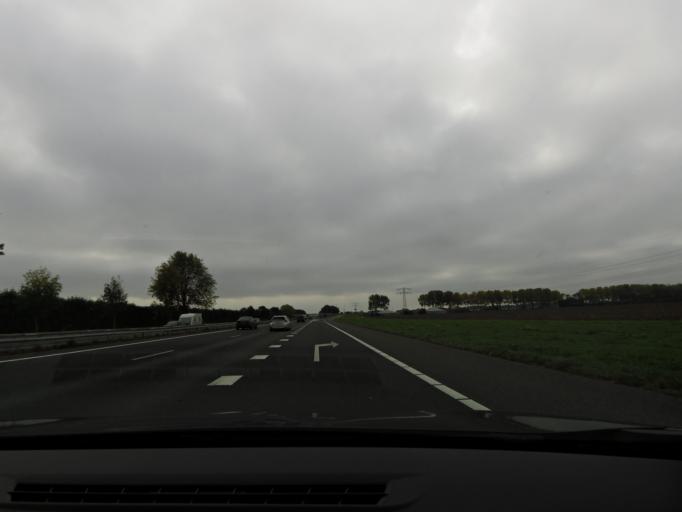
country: NL
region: South Holland
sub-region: Gemeente Oud-Beijerland
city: Oud-Beijerland
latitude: 51.7564
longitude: 4.4172
